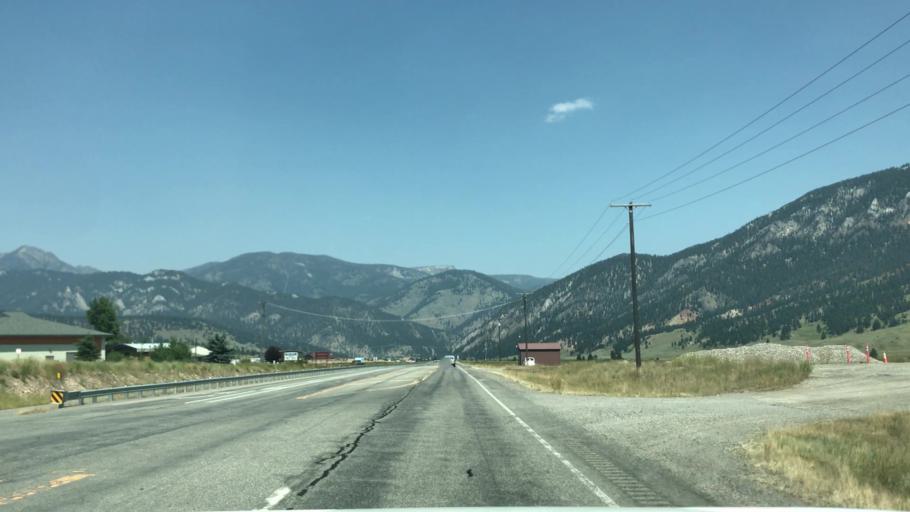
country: US
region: Montana
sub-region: Gallatin County
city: Big Sky
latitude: 45.2274
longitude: -111.2508
